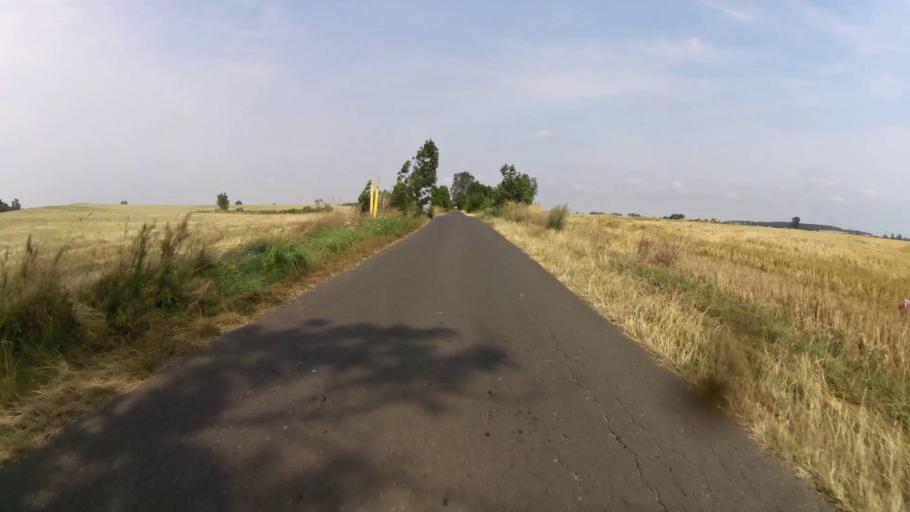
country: PL
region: West Pomeranian Voivodeship
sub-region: Powiat pyrzycki
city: Lipiany
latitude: 52.9803
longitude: 15.0323
